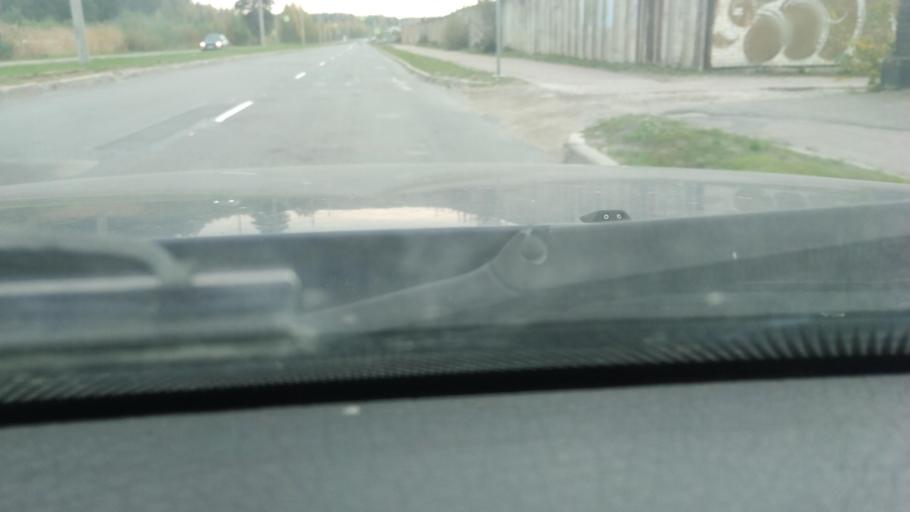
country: RU
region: Leningrad
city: Sosnovyy Bor
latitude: 59.9068
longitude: 29.1038
